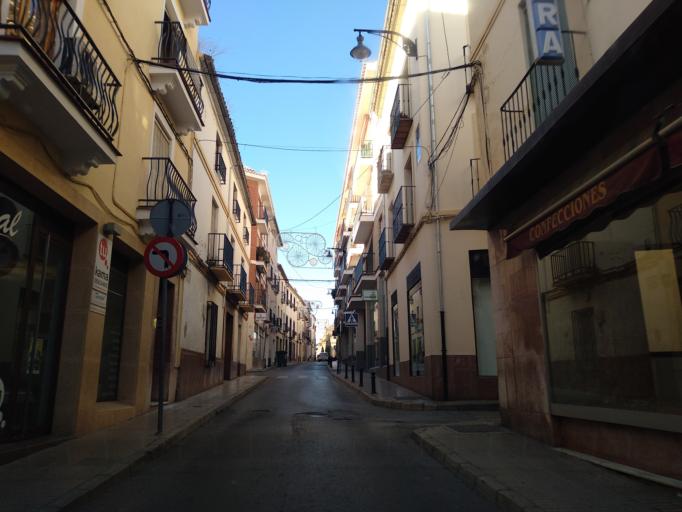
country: ES
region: Andalusia
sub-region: Provincia de Malaga
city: Antequera
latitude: 37.0202
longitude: -4.5589
